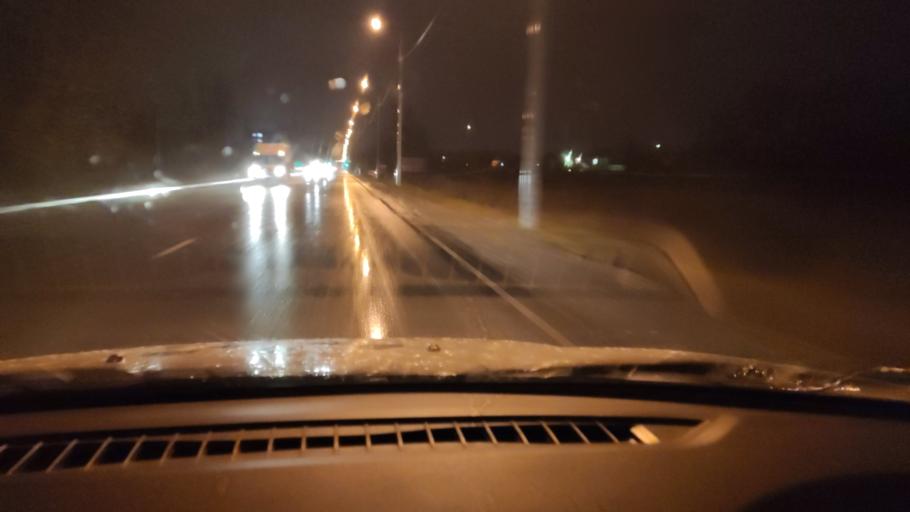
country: RU
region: Perm
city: Kondratovo
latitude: 57.9817
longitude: 56.1315
